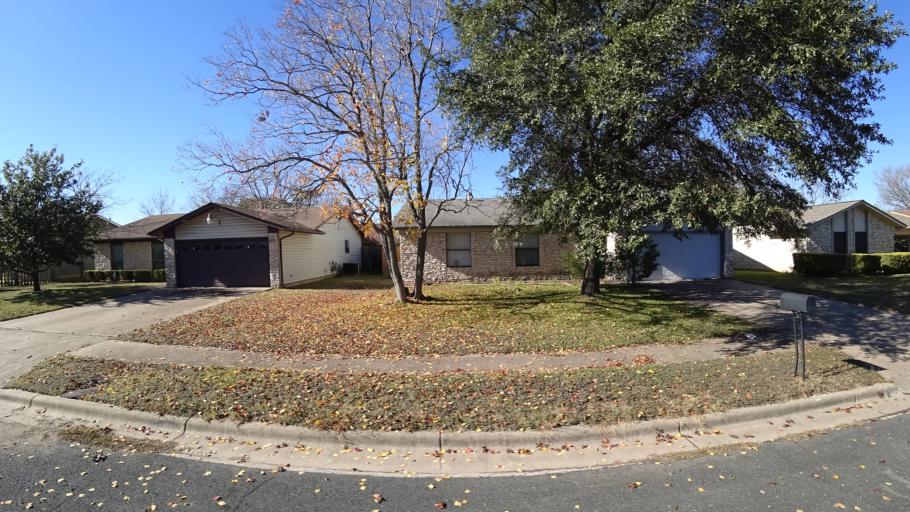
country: US
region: Texas
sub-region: Travis County
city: Wells Branch
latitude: 30.4249
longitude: -97.6899
